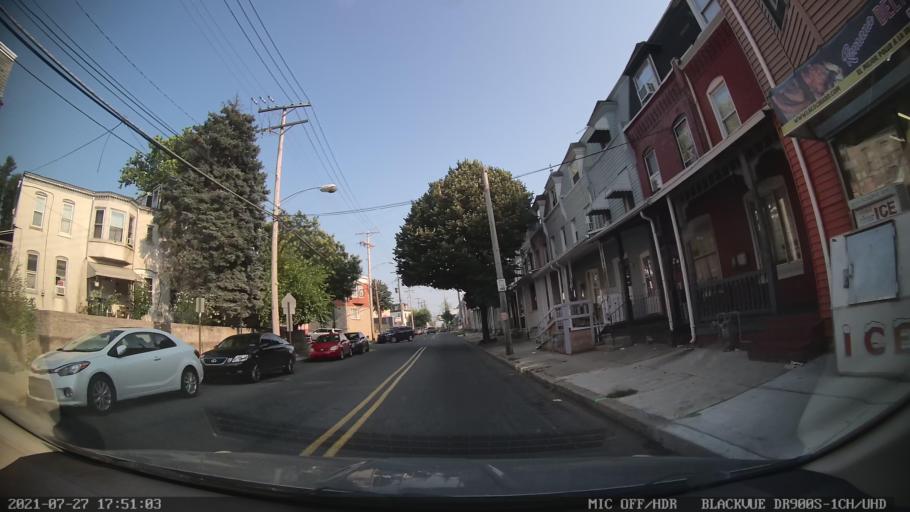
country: US
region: Pennsylvania
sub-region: Berks County
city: West Reading
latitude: 40.3480
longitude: -75.9418
